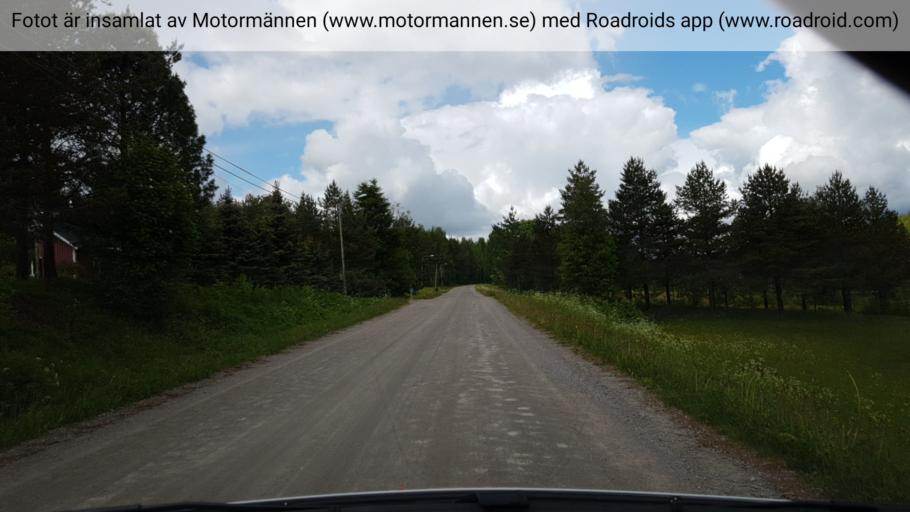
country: SE
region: Vaesterbotten
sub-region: Vannas Kommun
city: Vannasby
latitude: 63.8424
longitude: 19.9782
